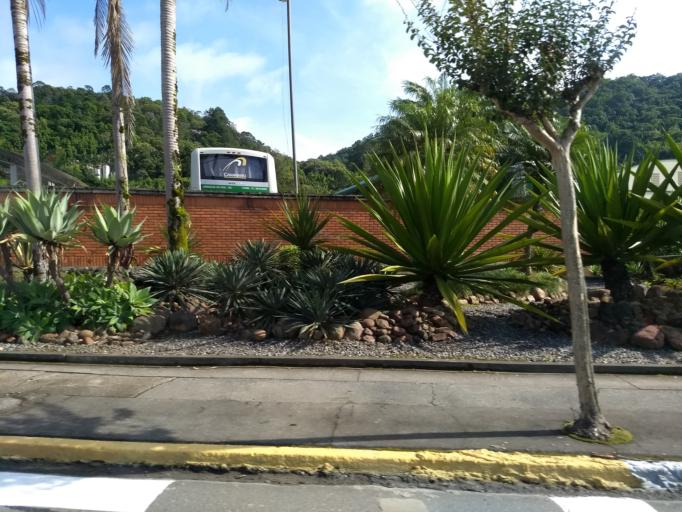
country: BR
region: Santa Catarina
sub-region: Jaragua Do Sul
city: Jaragua do Sul
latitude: -26.4706
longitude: -49.0924
